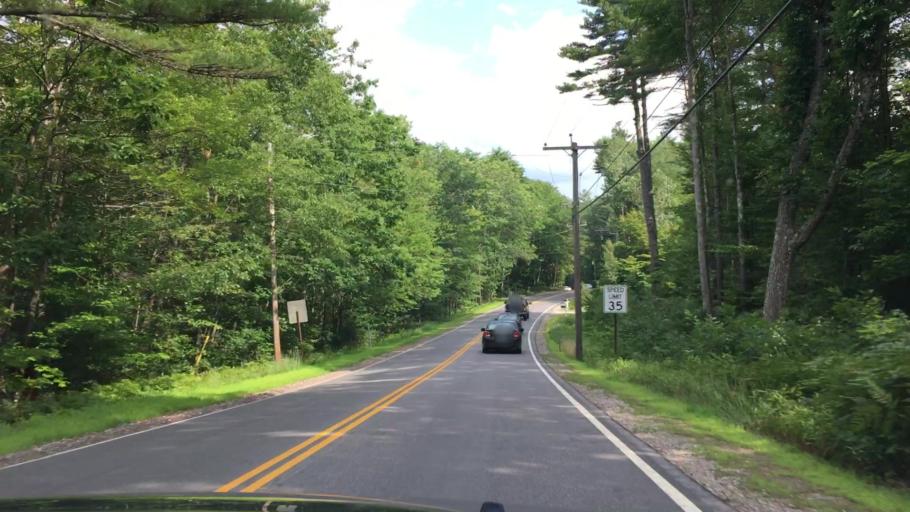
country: US
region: New Hampshire
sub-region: Belknap County
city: Gilford
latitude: 43.5852
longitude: -71.4159
